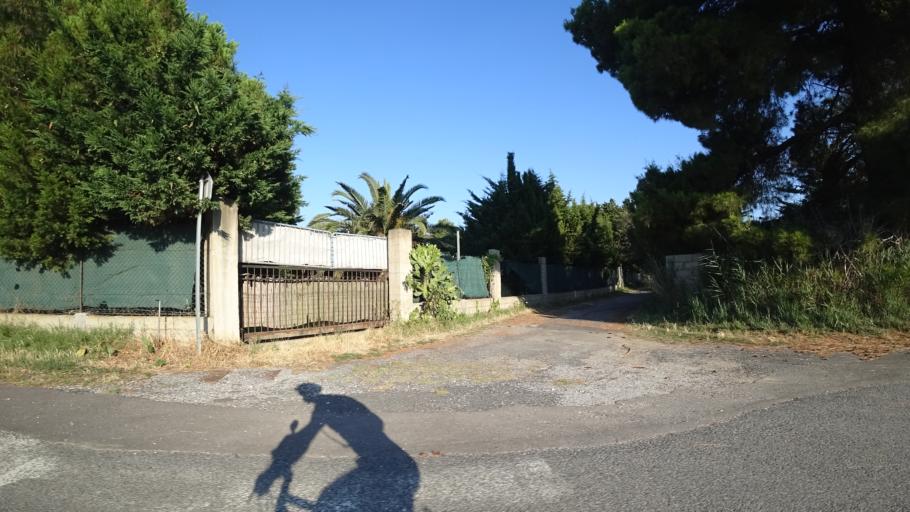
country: FR
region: Languedoc-Roussillon
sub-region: Departement des Pyrenees-Orientales
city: Sainte-Marie-Plage
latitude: 42.7212
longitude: 3.0295
